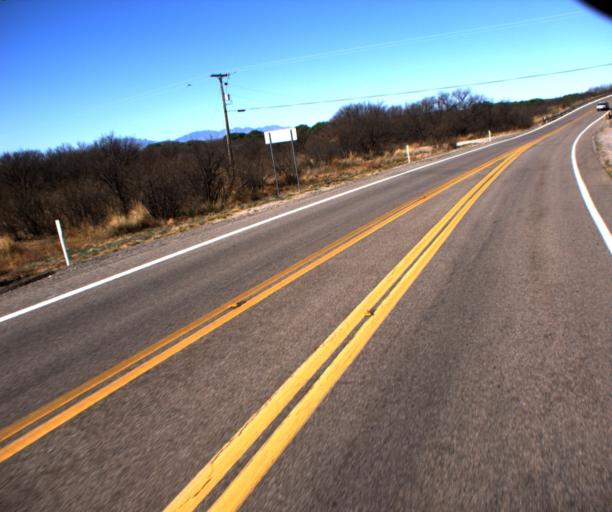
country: US
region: Arizona
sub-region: Cochise County
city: Tombstone
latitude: 31.7222
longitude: -110.1875
